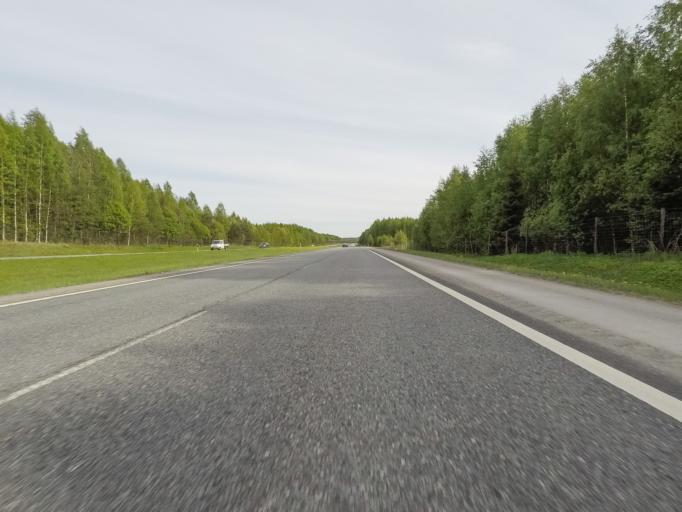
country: FI
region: Haeme
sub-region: Haemeenlinna
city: Janakkala
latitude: 60.8850
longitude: 24.5670
